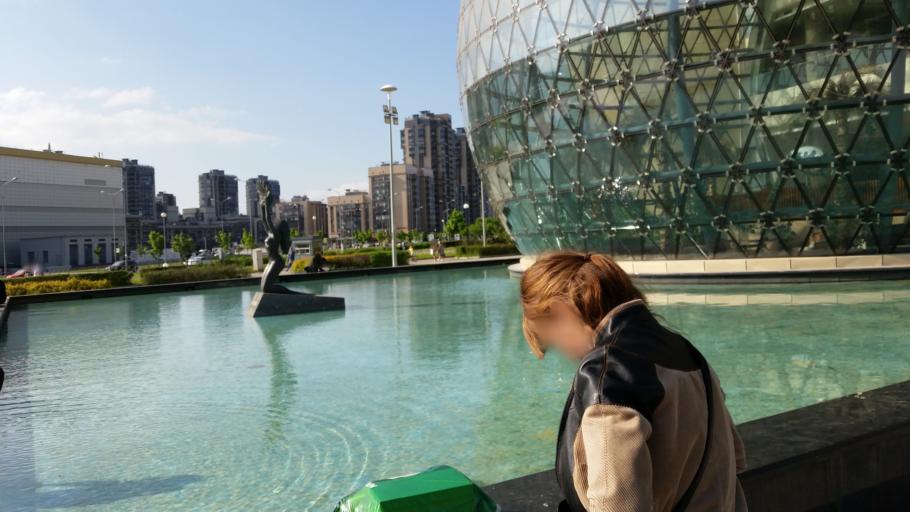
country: RU
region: St.-Petersburg
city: Sosnovaya Polyana
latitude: 59.8482
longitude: 30.1483
